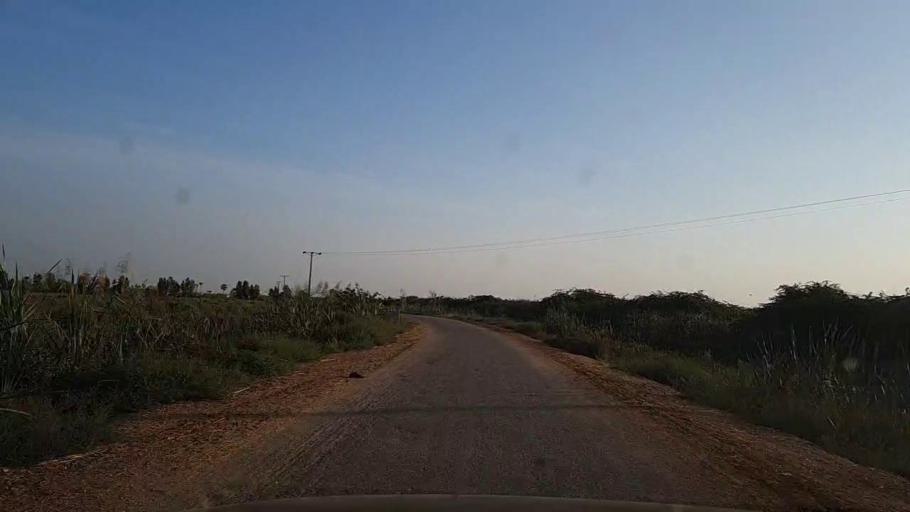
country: PK
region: Sindh
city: Thatta
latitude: 24.6326
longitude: 67.9117
